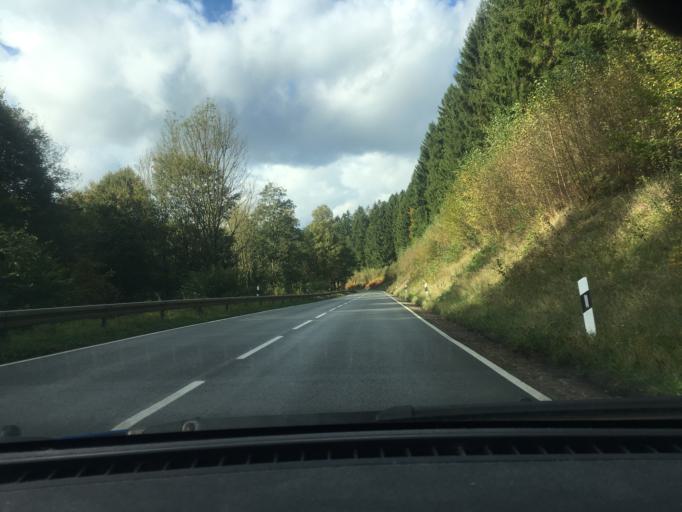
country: DE
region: Lower Saxony
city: Bevern
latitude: 51.7991
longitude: 9.5012
